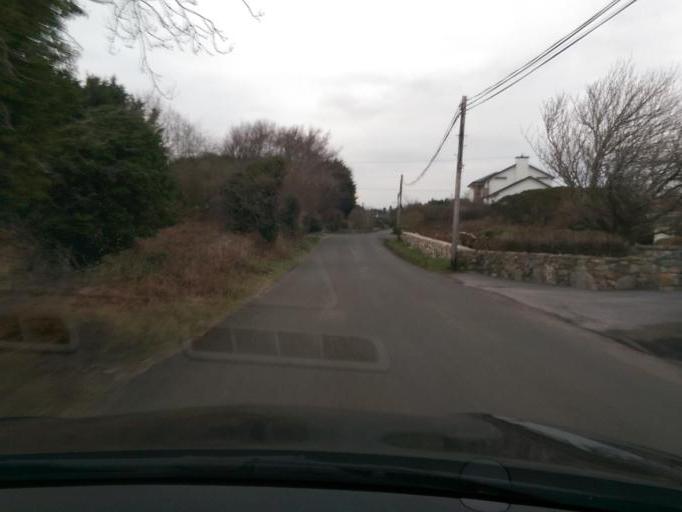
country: IE
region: Connaught
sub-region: County Galway
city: Bearna
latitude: 53.2543
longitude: -9.1534
